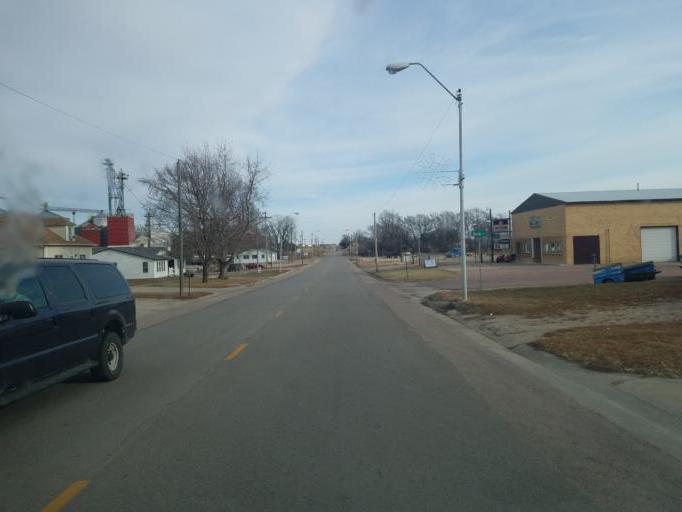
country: US
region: Nebraska
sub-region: Knox County
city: Creighton
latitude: 42.4667
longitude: -97.9022
